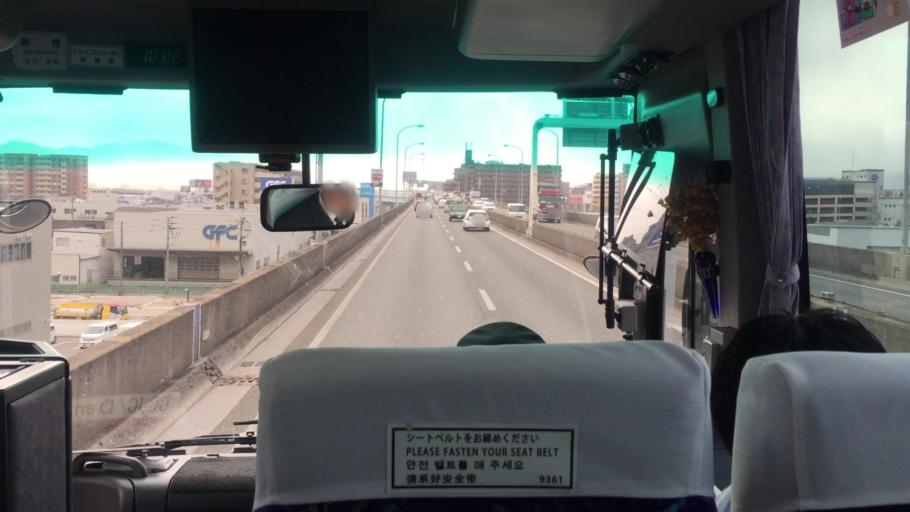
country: JP
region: Fukuoka
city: Fukuoka-shi
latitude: 33.5802
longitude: 130.4442
